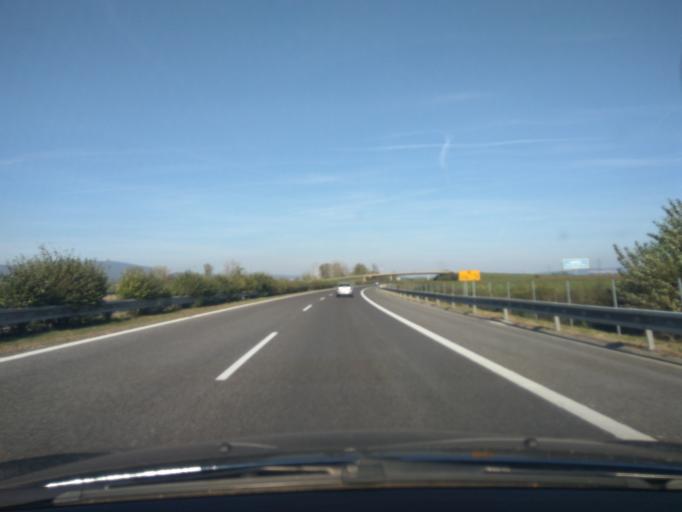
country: SK
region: Trenciansky
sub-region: Okres Nove Mesto nad Vahom
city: Nove Mesto nad Vahom
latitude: 48.8197
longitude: 17.9089
